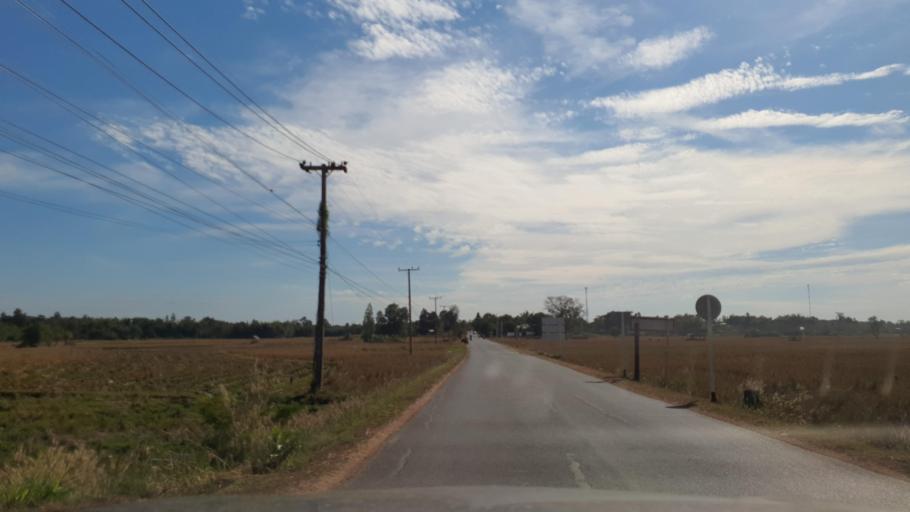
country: TH
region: Kalasin
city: Kuchinarai
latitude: 16.5532
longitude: 104.0976
